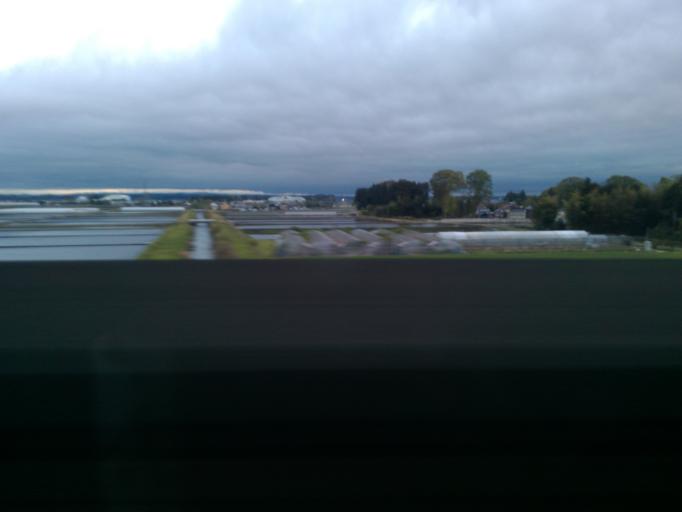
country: JP
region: Tochigi
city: Ujiie
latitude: 36.7189
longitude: 139.9262
